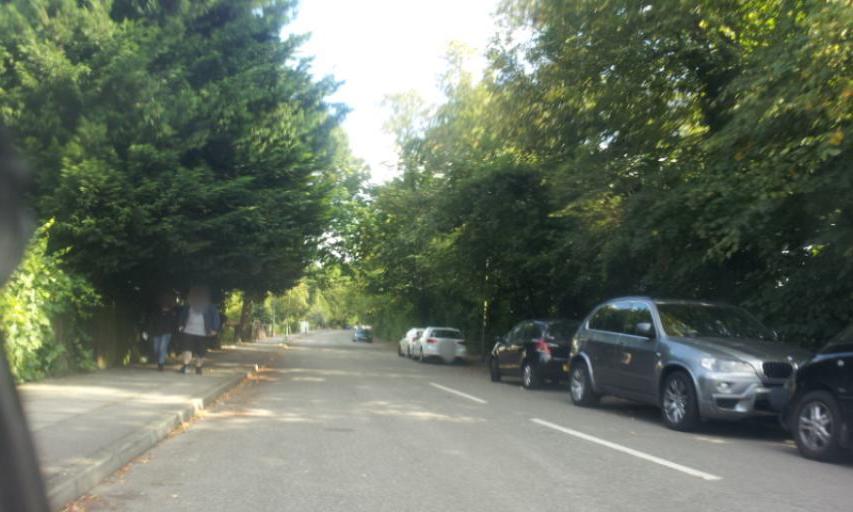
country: GB
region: England
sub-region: Greater London
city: Chislehurst
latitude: 51.3989
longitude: 0.0564
